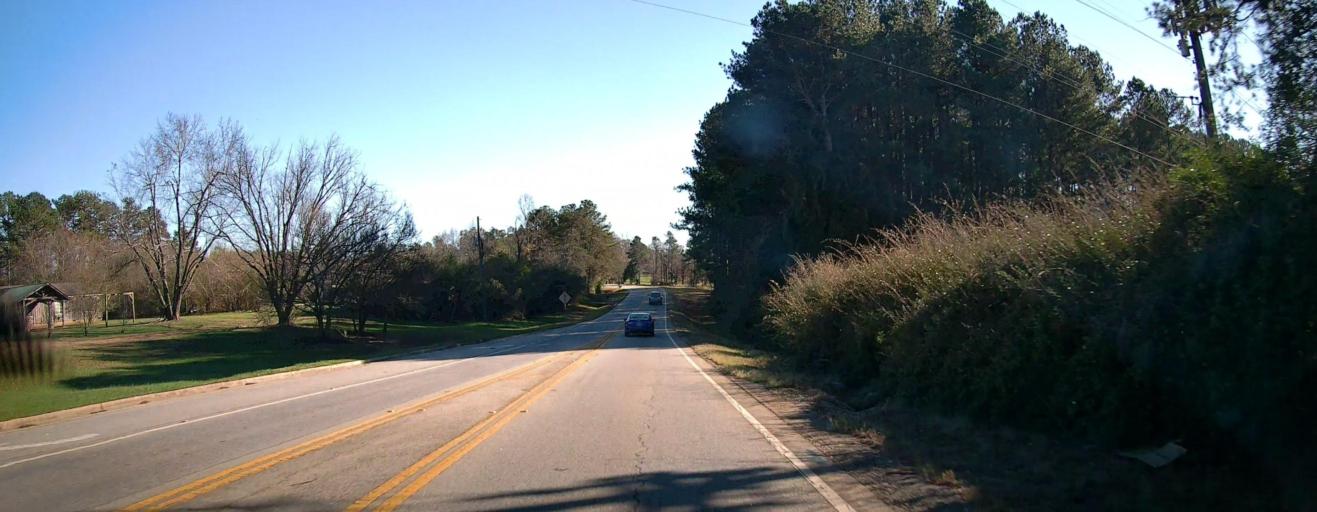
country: US
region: Georgia
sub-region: Hall County
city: Lula
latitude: 34.4038
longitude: -83.6985
